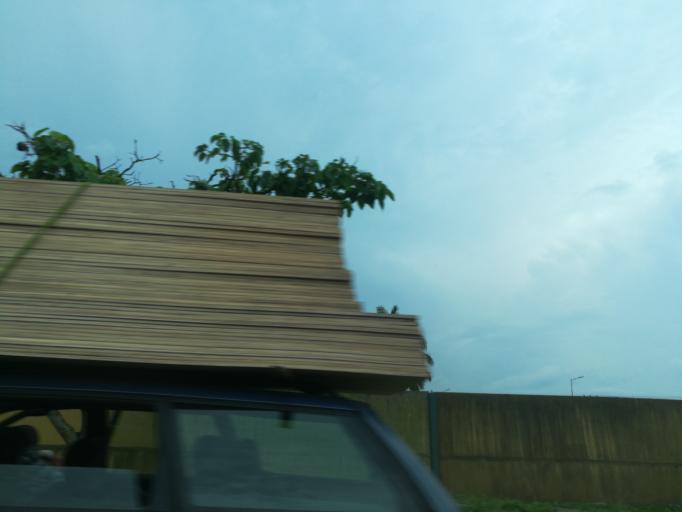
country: NG
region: Rivers
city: Port Harcourt
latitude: 4.7934
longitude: 7.0160
